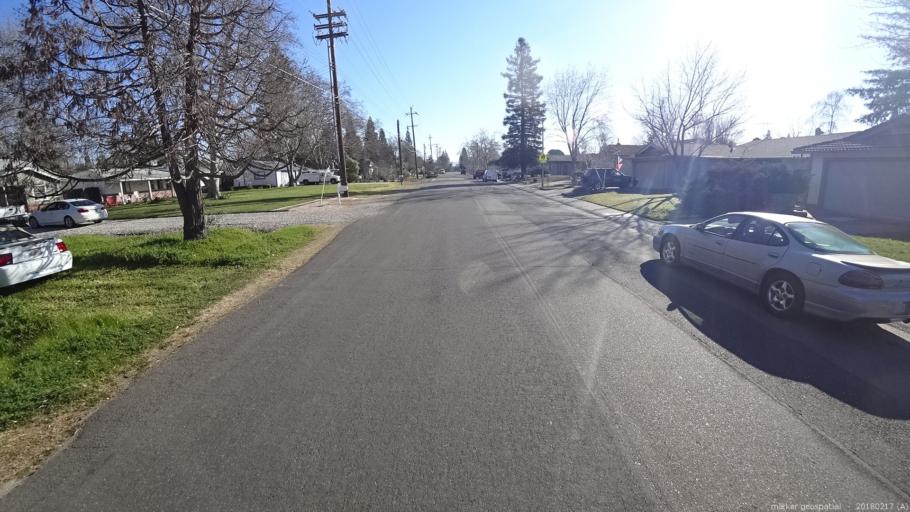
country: US
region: California
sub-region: Sacramento County
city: Orangevale
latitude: 38.6679
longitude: -121.2056
